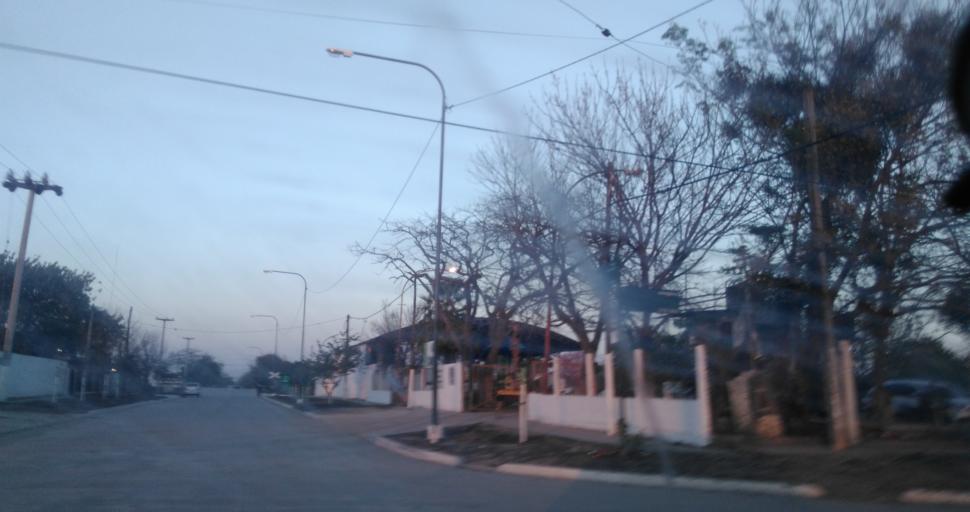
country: AR
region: Chaco
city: Resistencia
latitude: -27.4762
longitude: -58.9651
